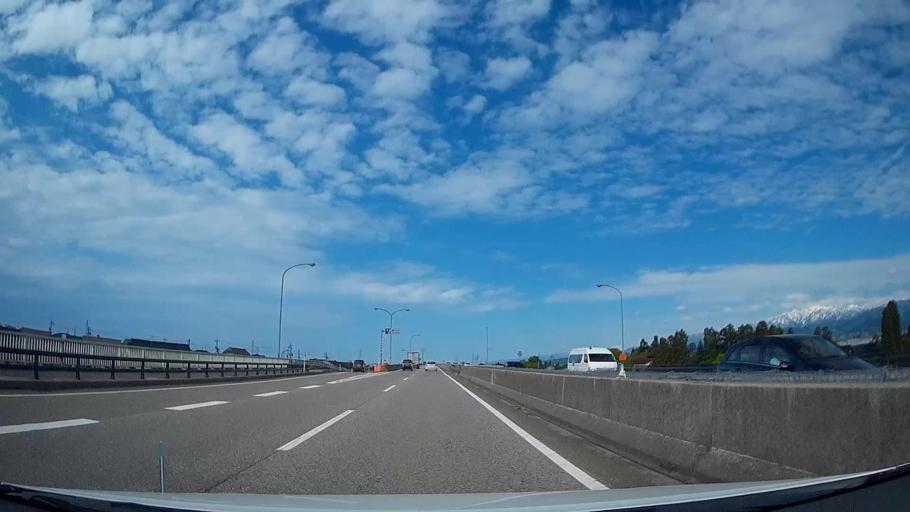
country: JP
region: Toyama
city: Namerikawa
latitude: 36.7390
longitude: 137.3406
